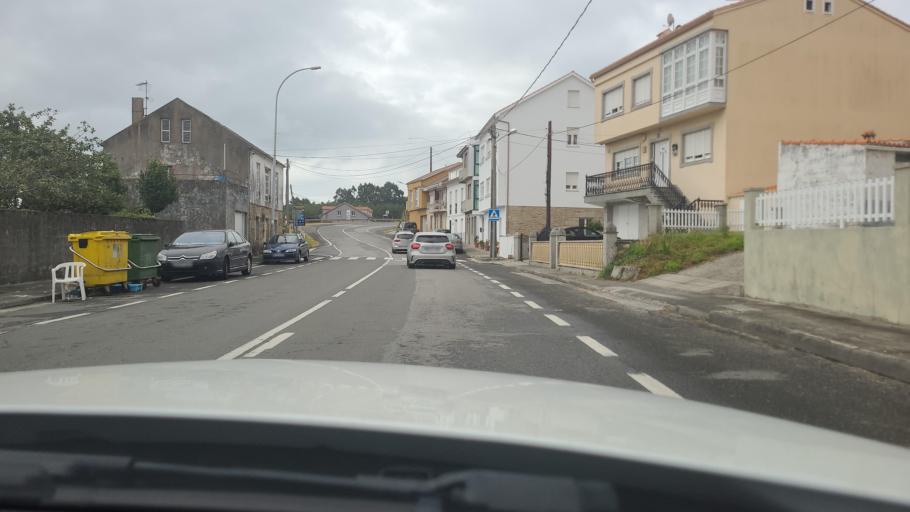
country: ES
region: Galicia
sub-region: Provincia da Coruna
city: Corcubion
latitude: 42.9412
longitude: -9.2352
